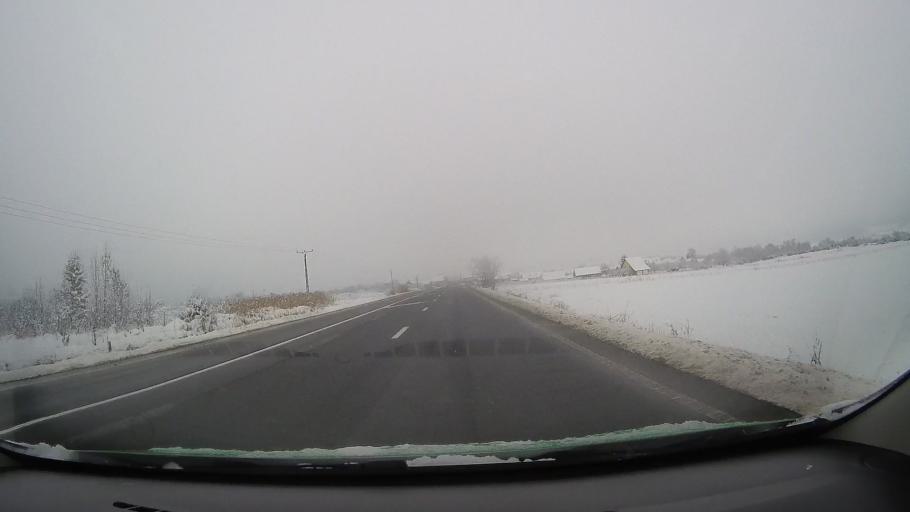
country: RO
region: Sibiu
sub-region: Oras Saliste
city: Saliste
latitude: 45.7874
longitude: 23.9305
